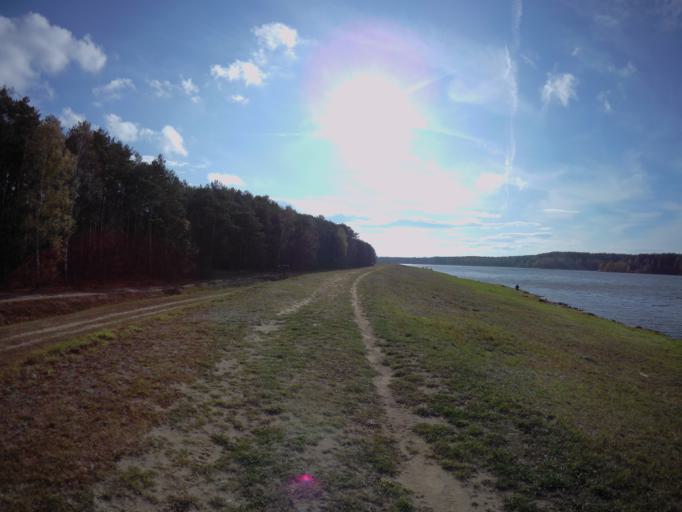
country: PL
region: Subcarpathian Voivodeship
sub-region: Powiat kolbuszowski
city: Lipnica
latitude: 50.3346
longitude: 21.9439
